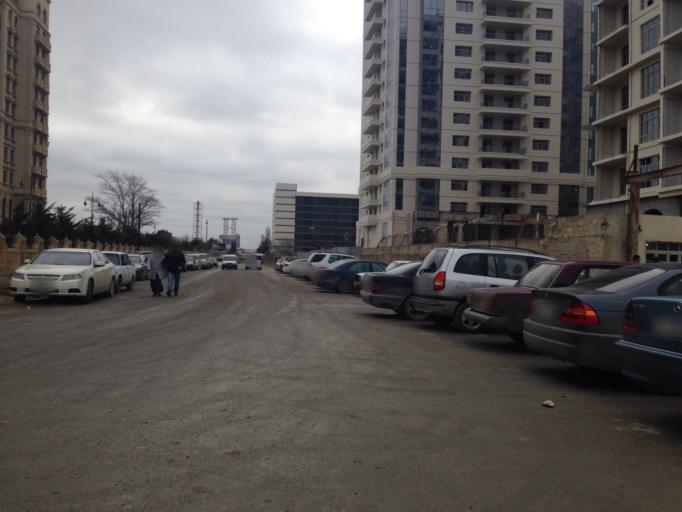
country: AZ
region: Baki
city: Sabuncu
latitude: 40.4197
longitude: 49.9096
